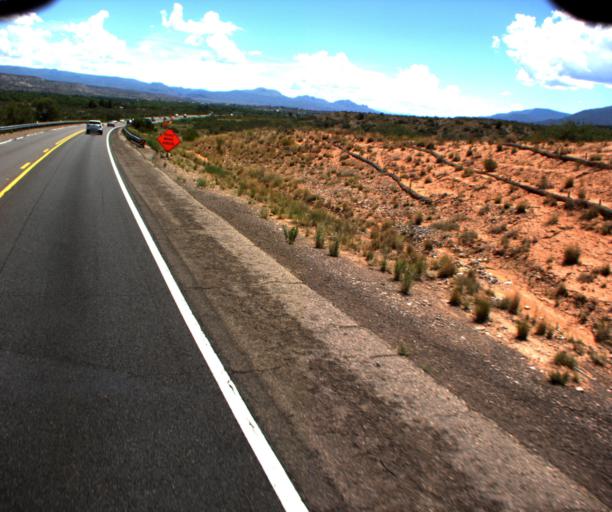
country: US
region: Arizona
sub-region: Yavapai County
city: Camp Verde
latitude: 34.5975
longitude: -111.8957
